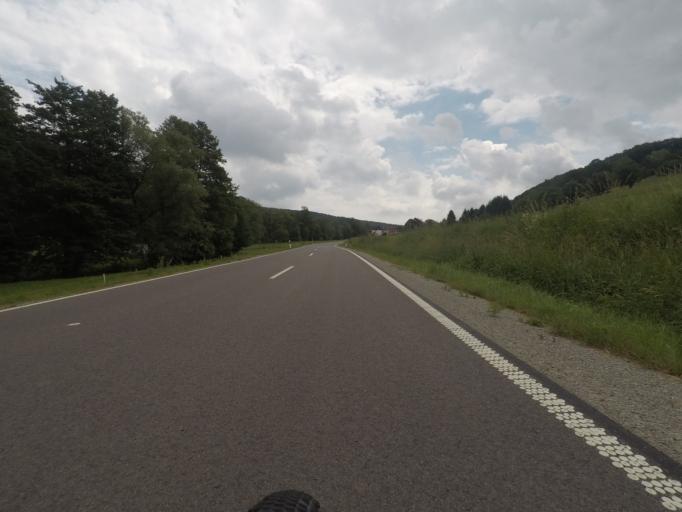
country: DE
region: Hesse
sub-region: Regierungsbezirk Kassel
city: Grossalmerode
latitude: 51.2070
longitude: 9.8198
